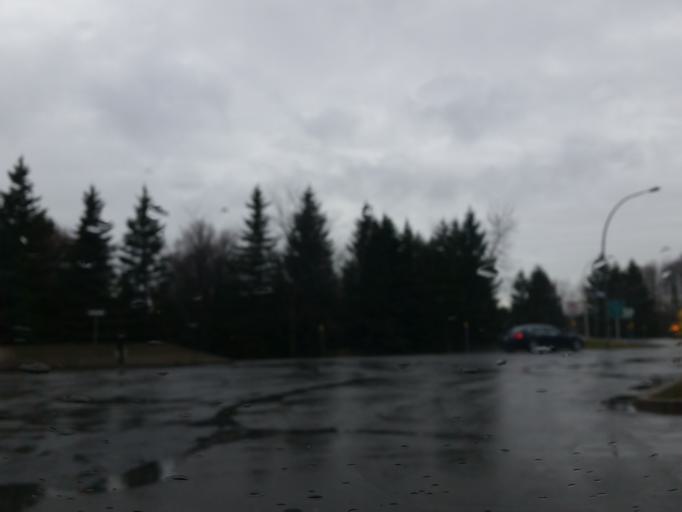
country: CA
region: Quebec
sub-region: Lanaudiere
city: Lavaltrie
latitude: 45.8913
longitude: -73.3495
